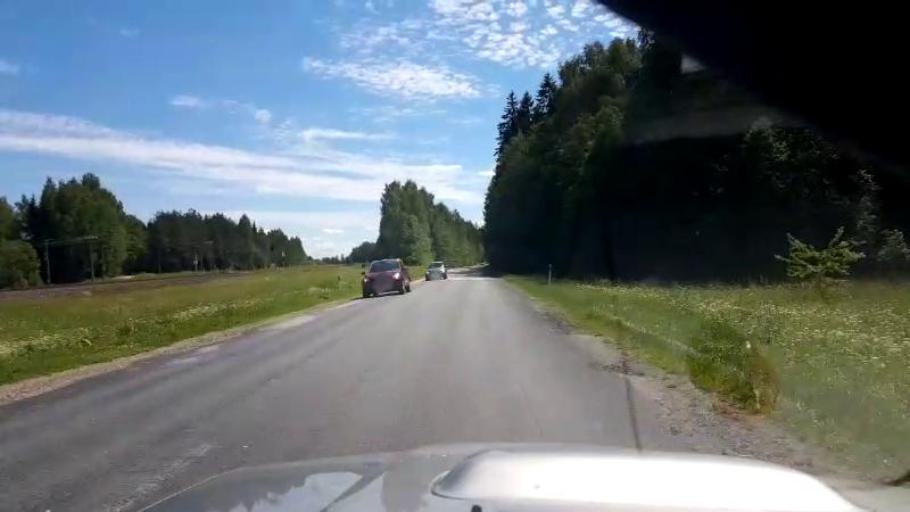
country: EE
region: Laeaene-Virumaa
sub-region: Rakke vald
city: Rakke
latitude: 58.8792
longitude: 26.2951
